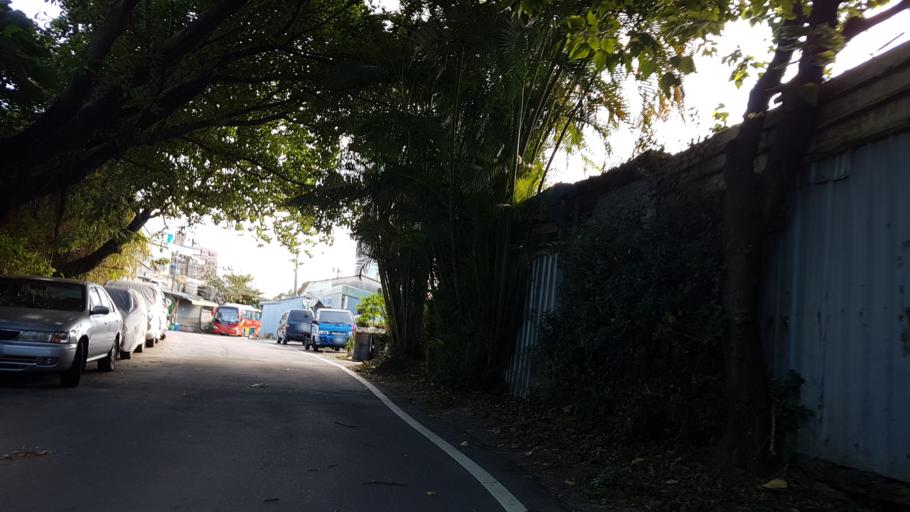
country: TW
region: Taipei
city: Taipei
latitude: 24.9920
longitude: 121.5322
